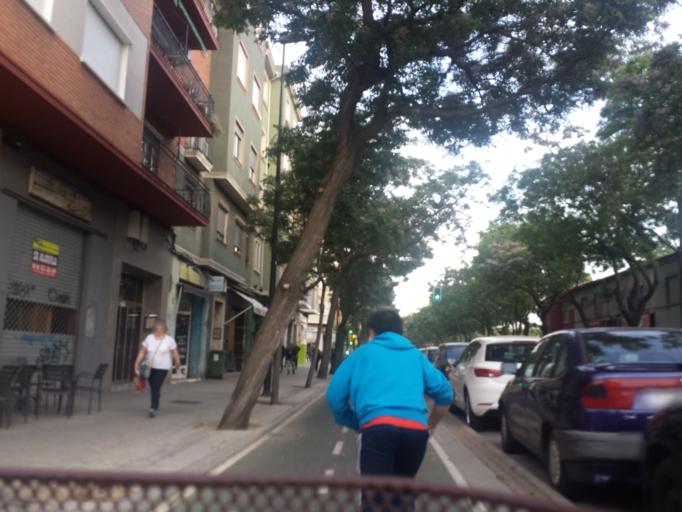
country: ES
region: Aragon
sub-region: Provincia de Zaragoza
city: Delicias
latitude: 41.6476
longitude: -0.9015
